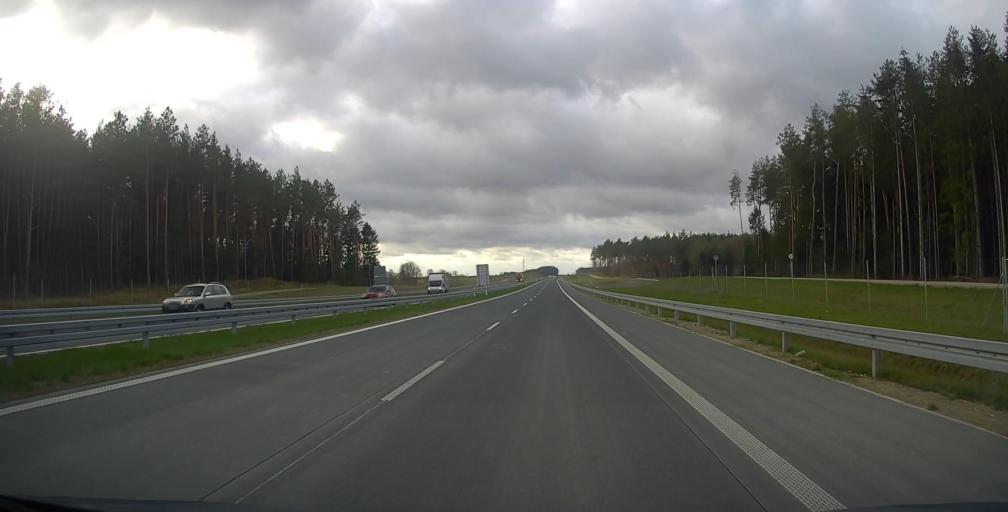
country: PL
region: Podlasie
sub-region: Powiat grajewski
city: Rajgrod
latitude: 53.8688
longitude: 22.6296
